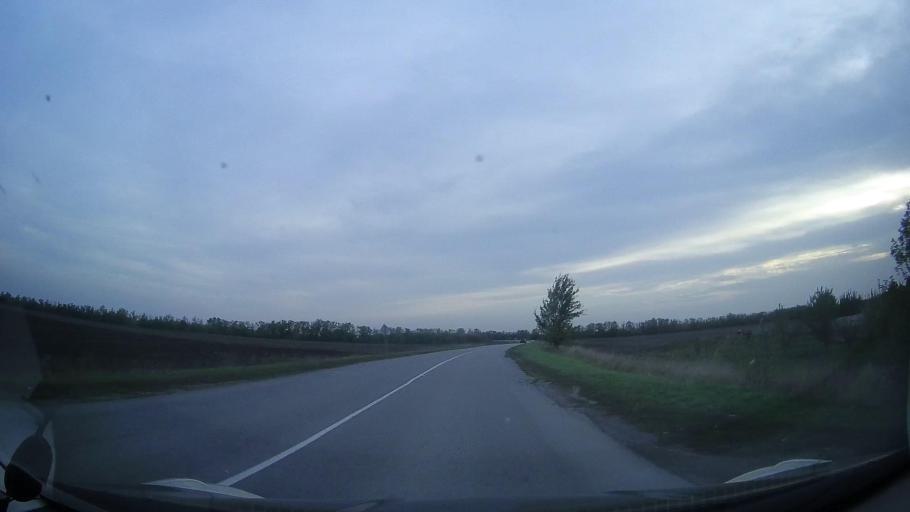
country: RU
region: Rostov
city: Kirovskaya
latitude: 47.0305
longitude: 39.9811
